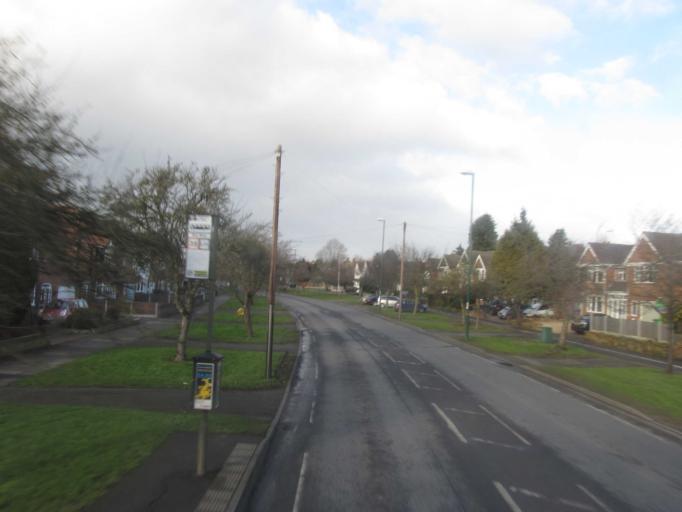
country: GB
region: England
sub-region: Nottinghamshire
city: Kimberley
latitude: 52.9444
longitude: -1.2246
